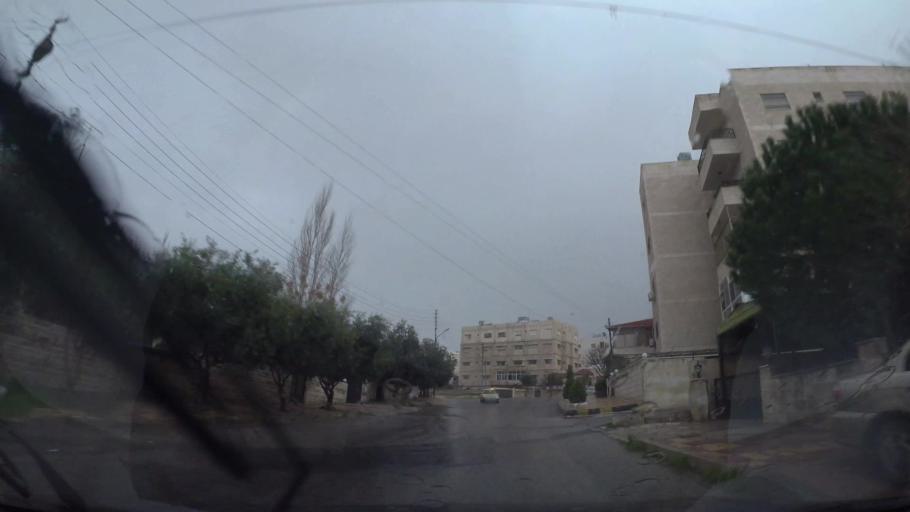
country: JO
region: Amman
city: Amman
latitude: 32.0045
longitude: 35.9591
